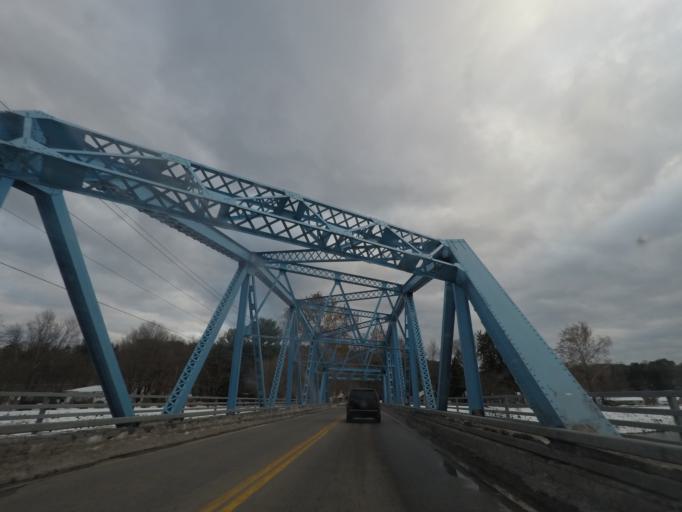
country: US
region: New York
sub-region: Ulster County
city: Rosendale Village
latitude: 41.8464
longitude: -74.0745
